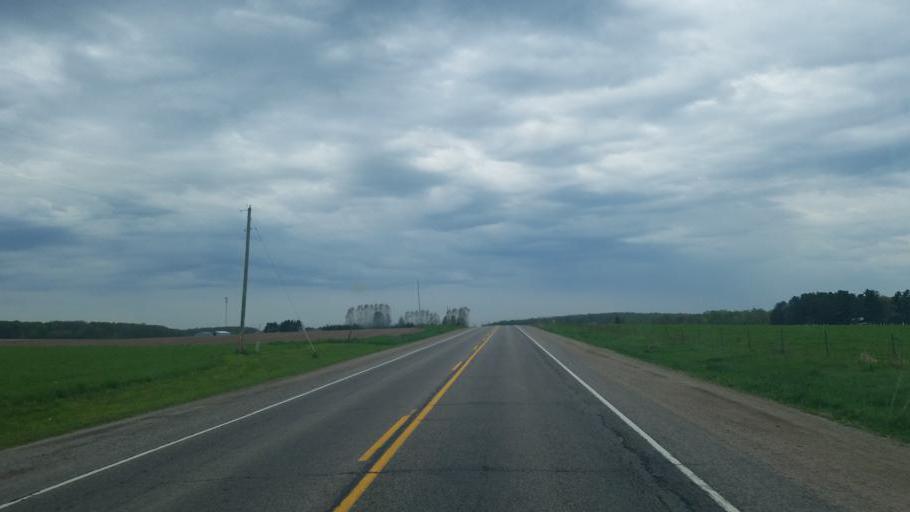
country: US
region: Wisconsin
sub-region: Marathon County
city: Spencer
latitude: 44.5990
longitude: -90.3184
